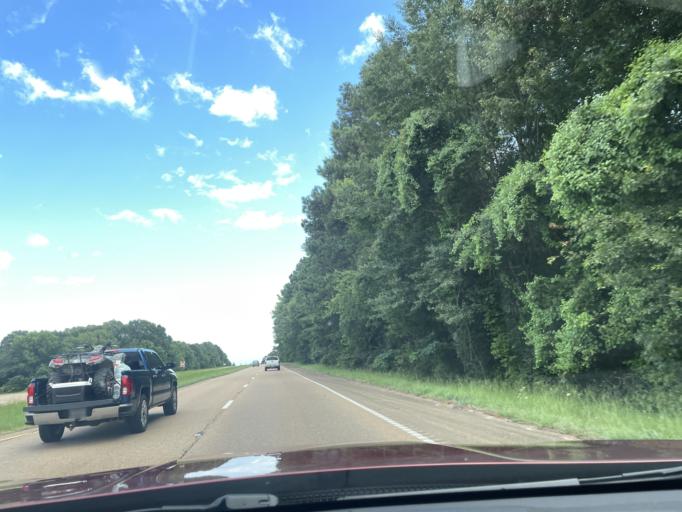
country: US
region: Mississippi
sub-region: Madison County
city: Flora
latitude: 32.5204
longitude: -90.3071
